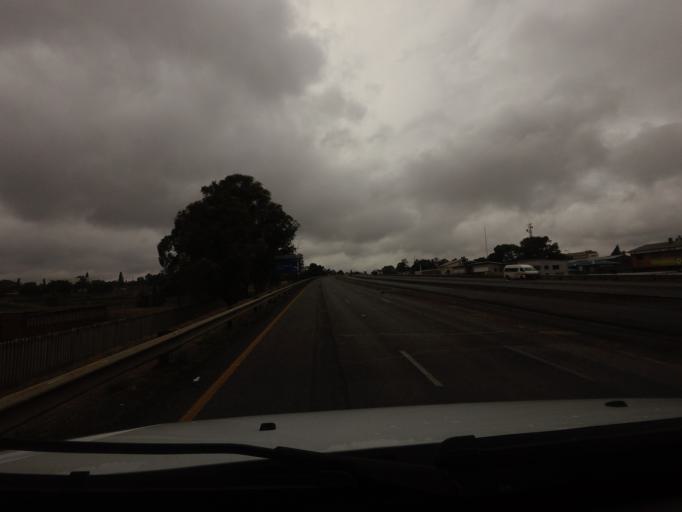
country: ZA
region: Mpumalanga
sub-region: Nkangala District Municipality
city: Witbank
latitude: -25.8849
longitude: 29.2146
